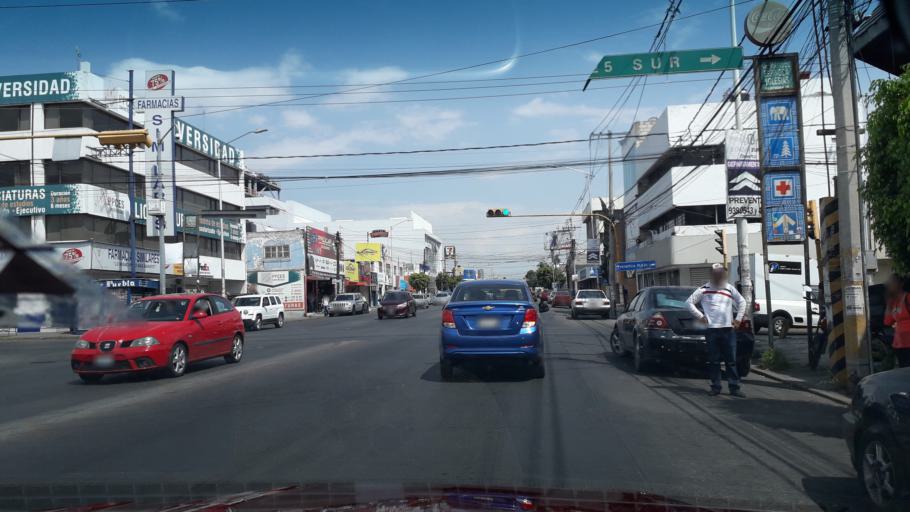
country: MX
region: Puebla
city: Puebla
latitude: 19.0419
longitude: -98.2235
